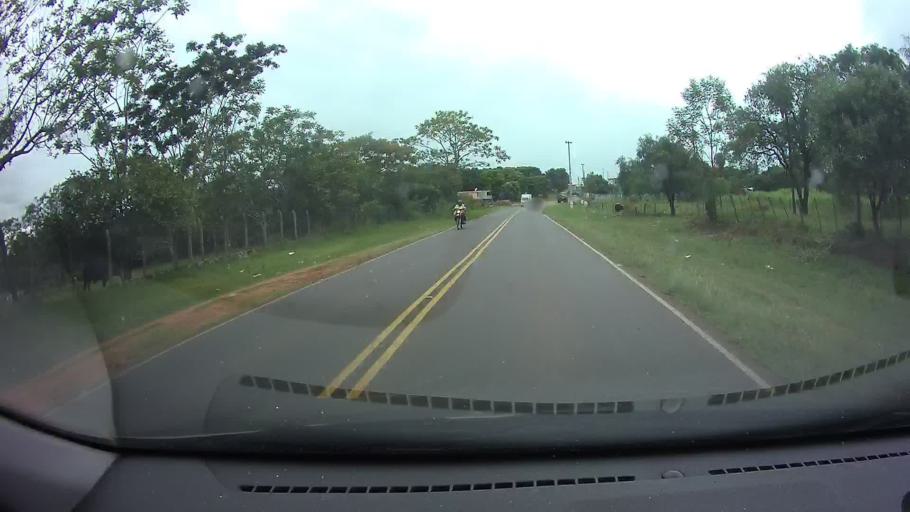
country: PY
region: Paraguari
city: Carapegua
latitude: -25.7553
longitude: -57.2577
